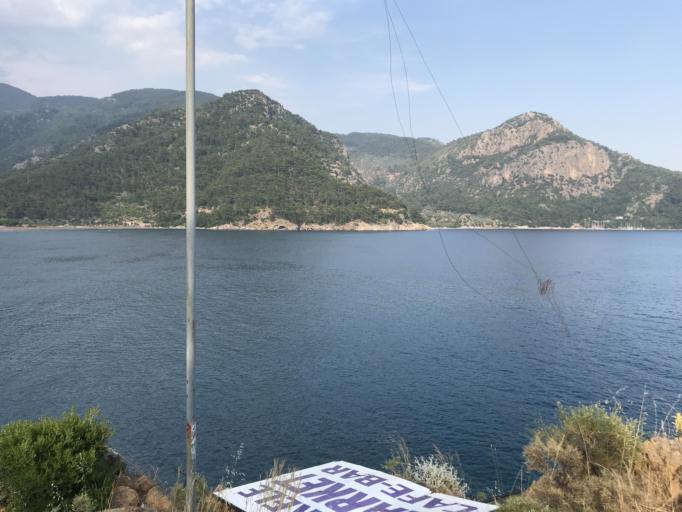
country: TR
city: Dalyan
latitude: 36.8273
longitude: 28.5499
